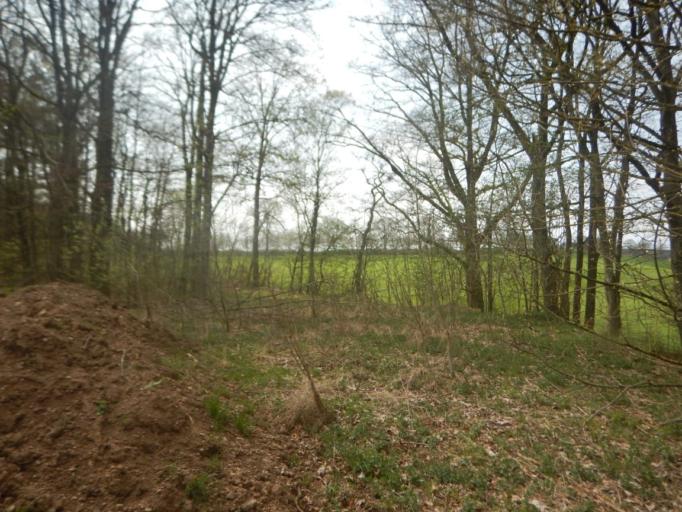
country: LU
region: Diekirch
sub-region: Canton de Clervaux
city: Clervaux
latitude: 50.0592
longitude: 6.0132
